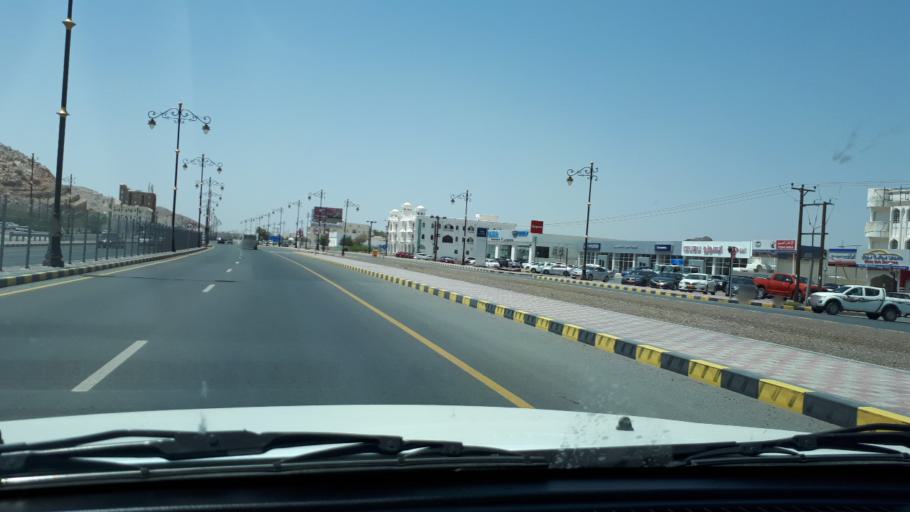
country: OM
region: Muhafazat ad Dakhiliyah
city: Nizwa
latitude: 22.9034
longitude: 57.5331
